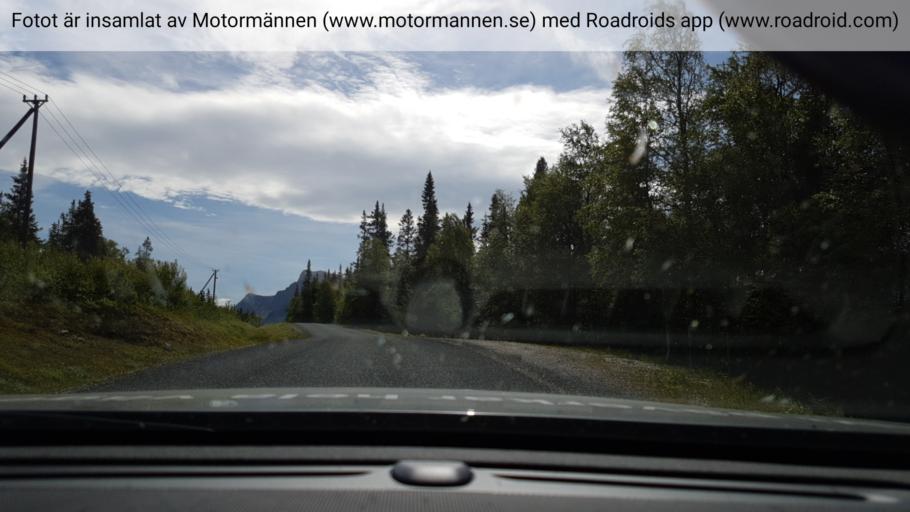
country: SE
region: Vaesterbotten
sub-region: Vilhelmina Kommun
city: Sjoberg
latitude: 65.2699
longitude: 15.3685
